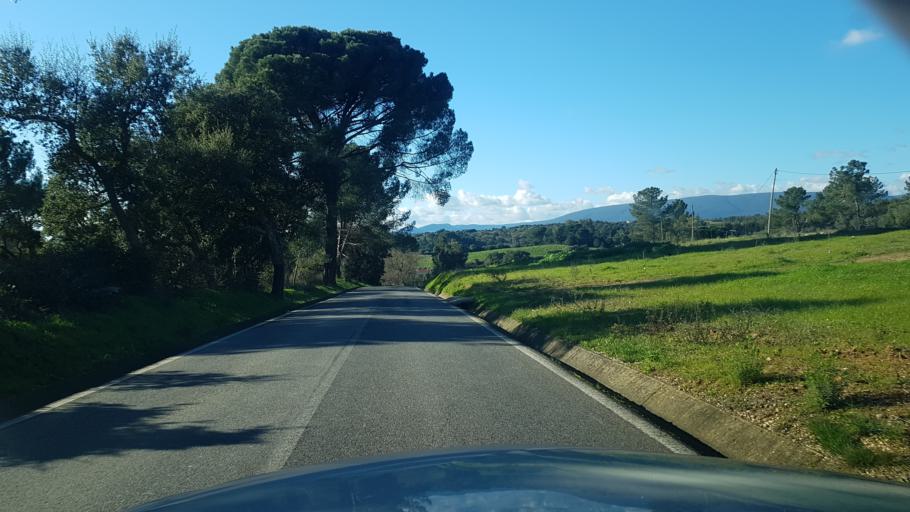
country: PT
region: Santarem
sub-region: Torres Novas
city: Torres Novas
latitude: 39.4768
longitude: -8.5088
